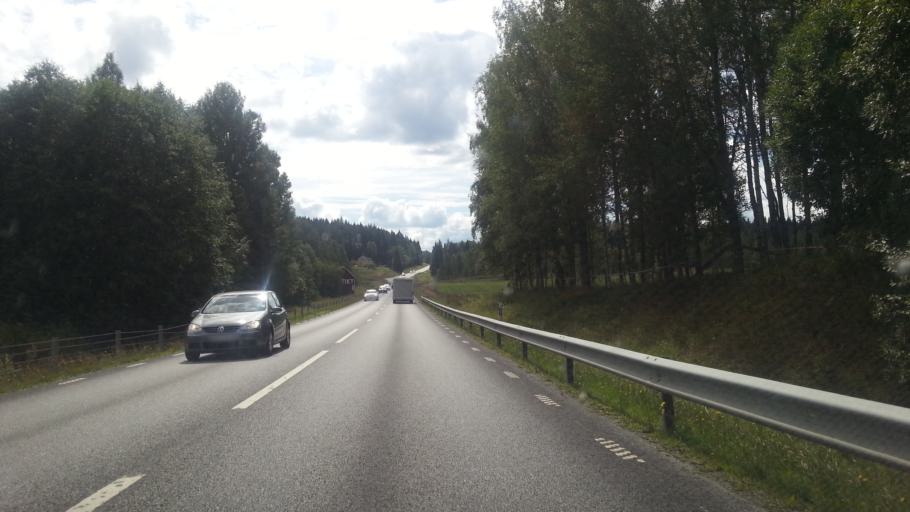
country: SE
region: OErebro
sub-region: Lindesbergs Kommun
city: Stora
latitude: 59.6811
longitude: 15.0986
